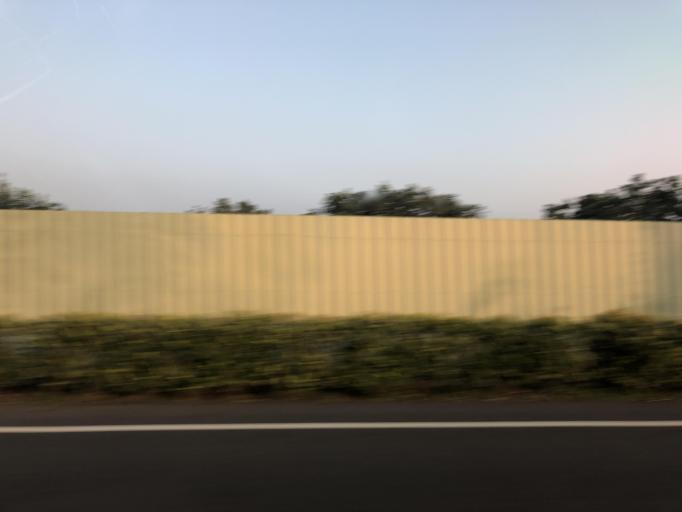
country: TW
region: Taiwan
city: Xinying
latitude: 23.1964
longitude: 120.2641
